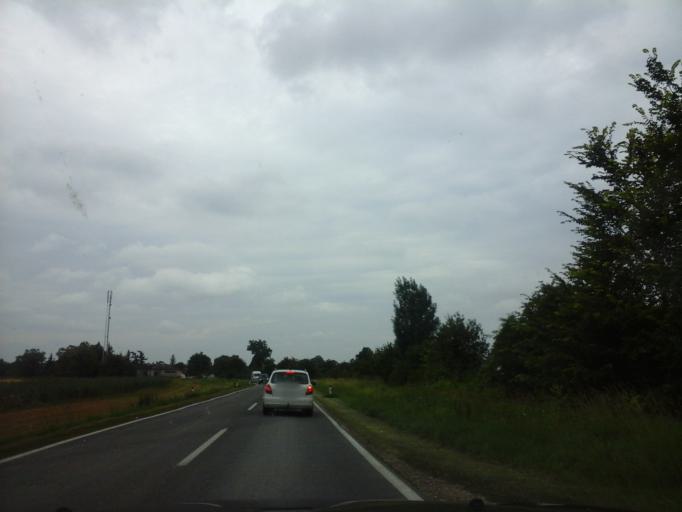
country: AT
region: Lower Austria
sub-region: Politischer Bezirk Ganserndorf
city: Eckartsau
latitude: 48.1698
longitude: 16.8207
